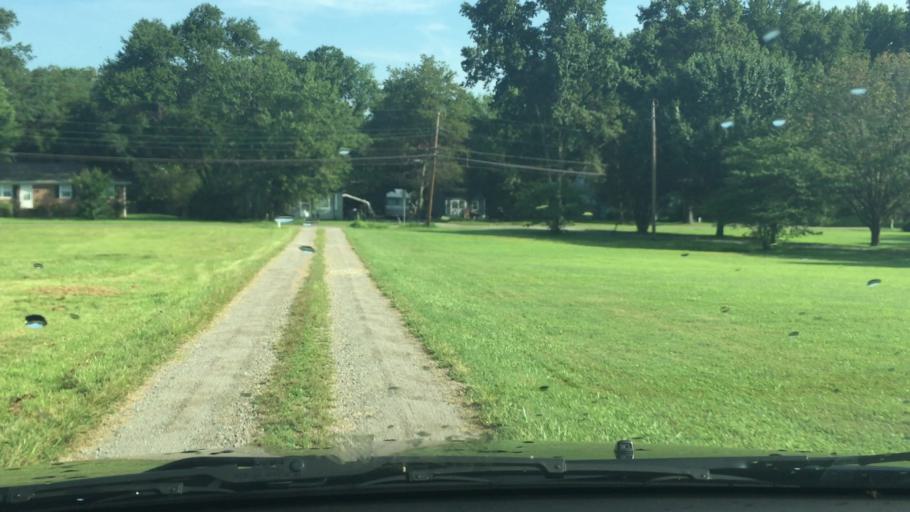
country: US
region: Virginia
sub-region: Hanover County
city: Ashland
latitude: 37.7525
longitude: -77.4968
